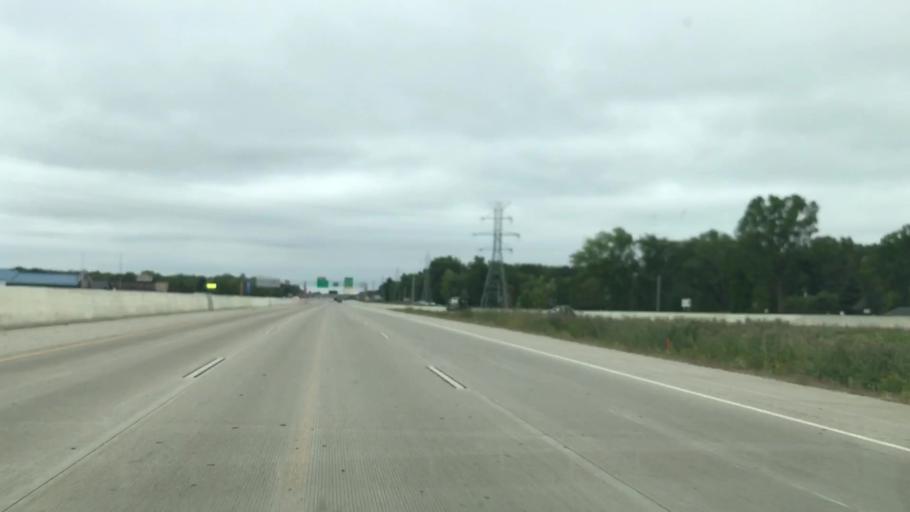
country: US
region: Wisconsin
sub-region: Brown County
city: Suamico
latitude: 44.5895
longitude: -88.0487
